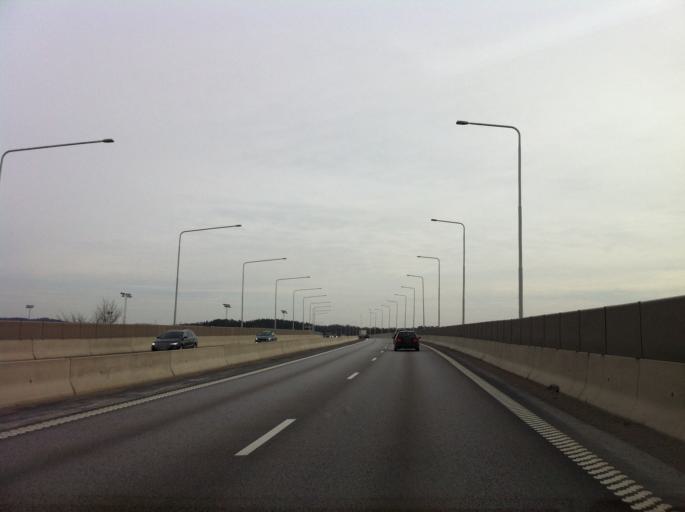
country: SE
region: Vaestra Goetaland
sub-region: Kungalvs Kommun
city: Kode
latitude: 57.9061
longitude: 11.9050
